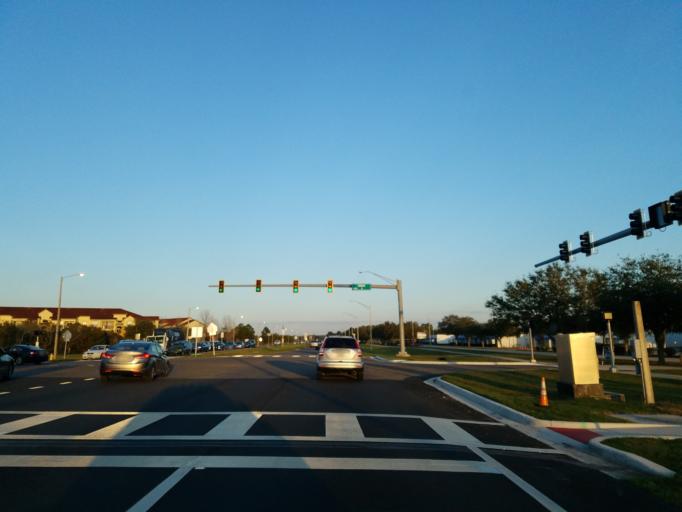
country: US
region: Florida
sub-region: Hillsborough County
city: Pebble Creek
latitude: 28.1420
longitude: -82.3263
